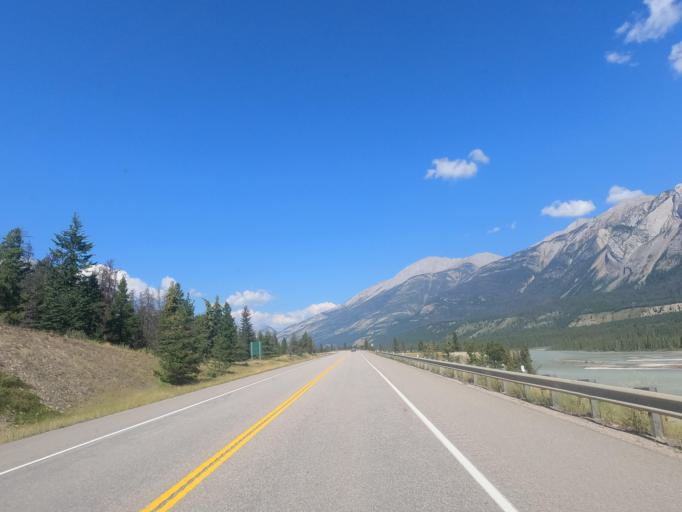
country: CA
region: Alberta
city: Jasper Park Lodge
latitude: 52.9448
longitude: -118.0394
